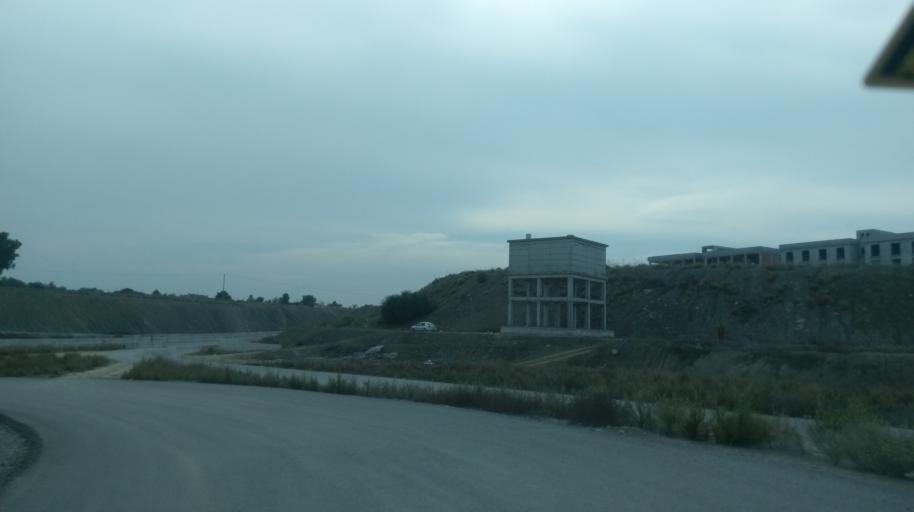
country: CY
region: Lefkosia
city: Nicosia
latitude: 35.2362
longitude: 33.3249
